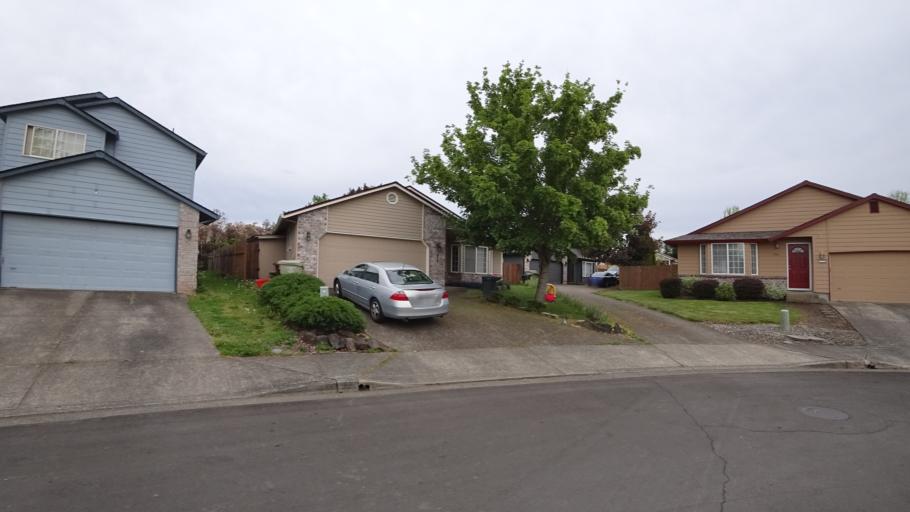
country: US
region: Oregon
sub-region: Washington County
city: Aloha
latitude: 45.5150
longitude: -122.9094
